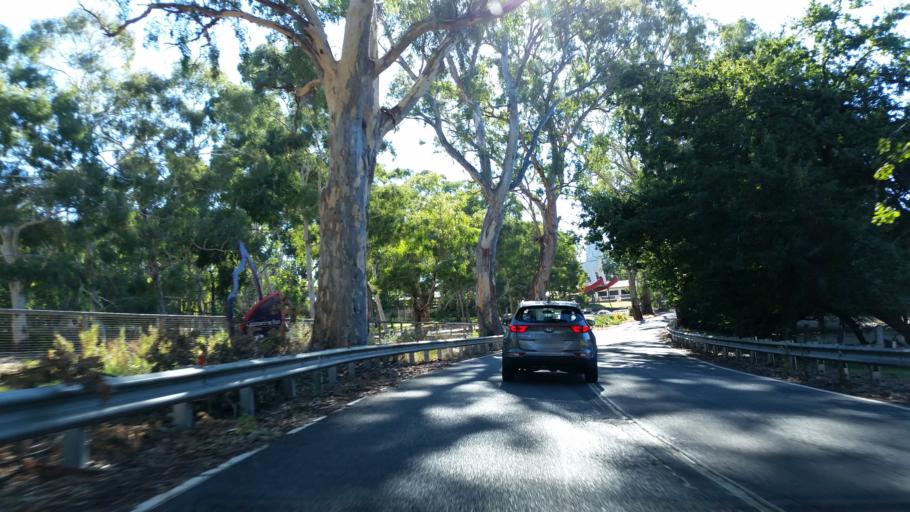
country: AU
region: South Australia
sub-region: Adelaide Hills
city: Gumeracha
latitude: -34.8218
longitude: 138.8937
